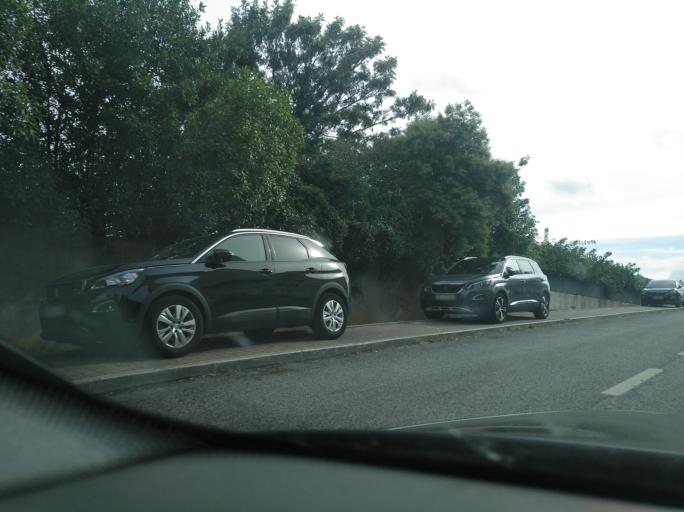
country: PT
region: Lisbon
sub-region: Amadora
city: Amadora
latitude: 38.7369
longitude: -9.2206
